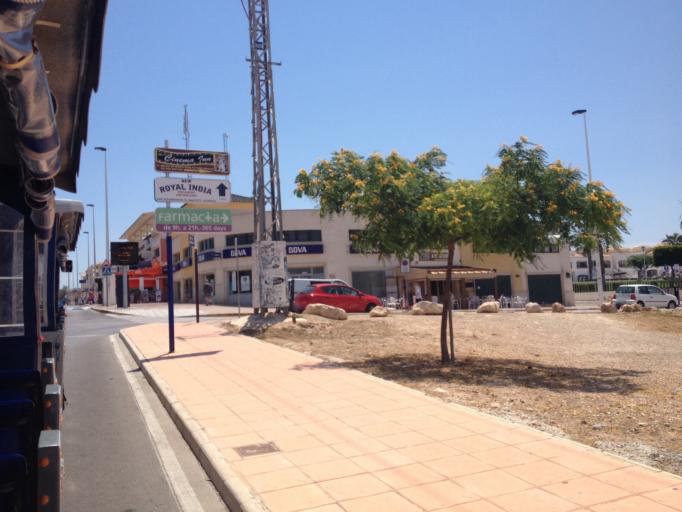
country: ES
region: Valencia
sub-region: Provincia de Alicante
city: Santa Pola
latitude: 38.2272
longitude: -0.5240
